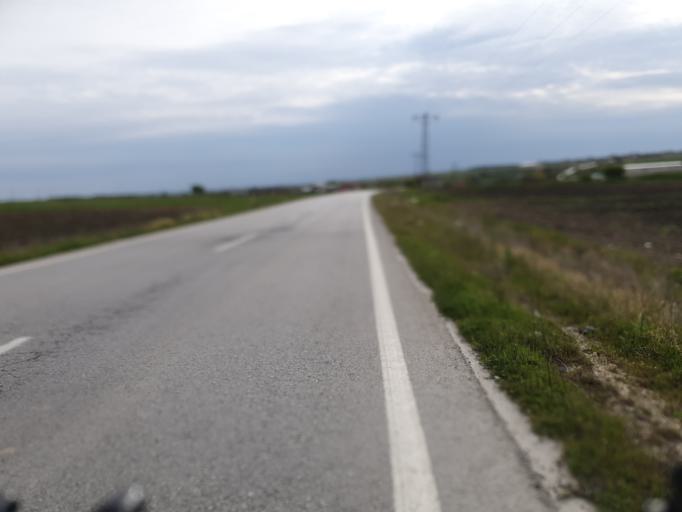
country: TR
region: Tekirdag
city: Velimese
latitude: 41.2923
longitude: 27.9286
